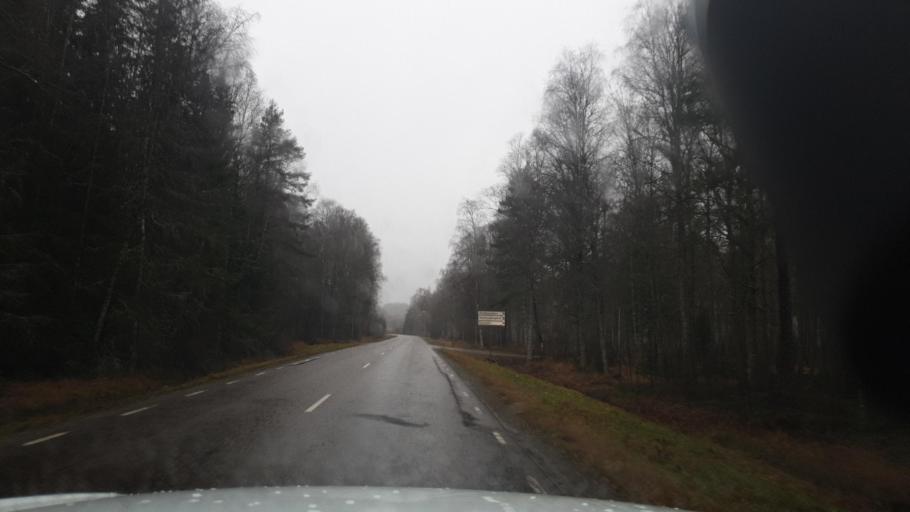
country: SE
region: Vaermland
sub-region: Arvika Kommun
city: Arvika
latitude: 59.6574
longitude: 12.8875
